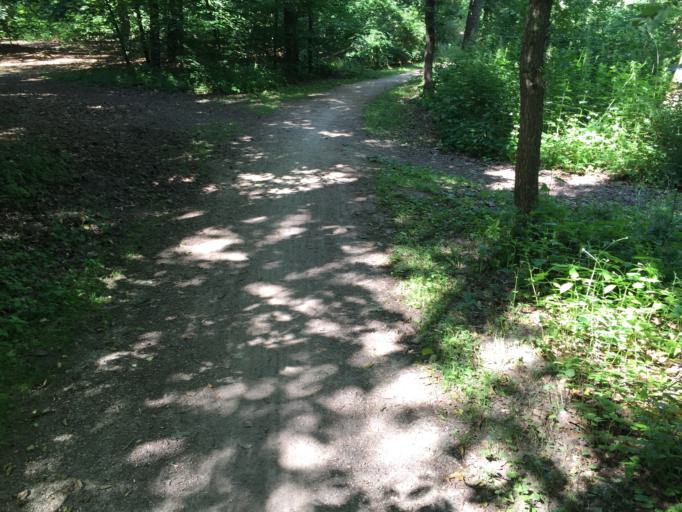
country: NL
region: Utrecht
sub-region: Gemeente Zeist
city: Zeist
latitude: 52.0844
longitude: 5.2660
